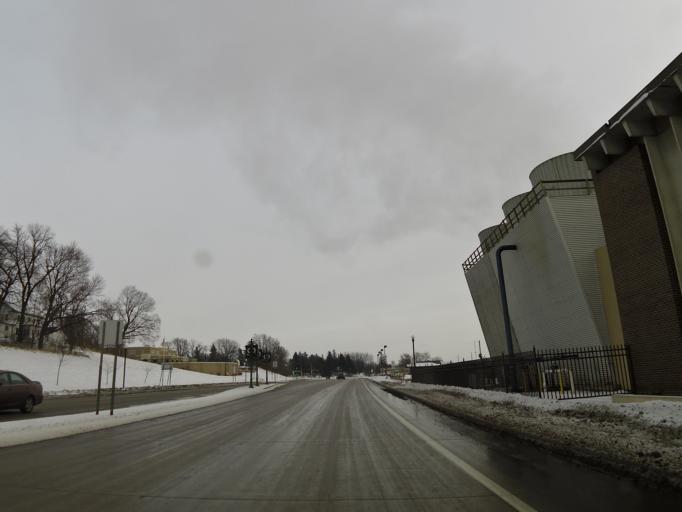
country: US
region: Minnesota
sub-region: McLeod County
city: Hutchinson
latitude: 44.8962
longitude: -94.3680
